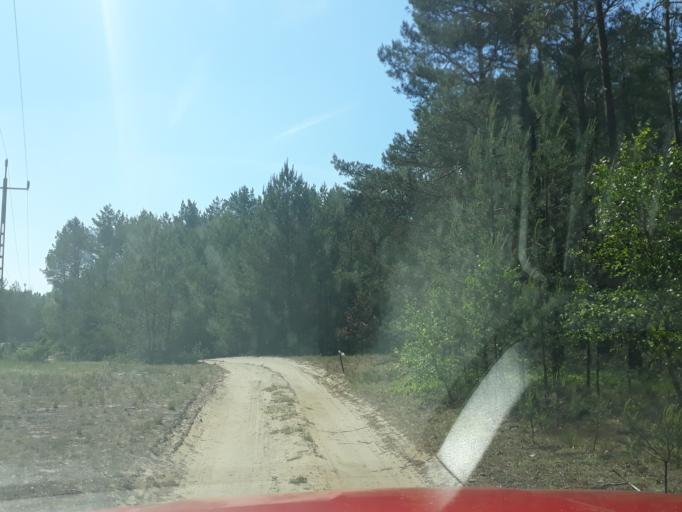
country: PL
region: Pomeranian Voivodeship
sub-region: Powiat chojnicki
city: Chojnice
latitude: 53.8722
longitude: 17.5395
